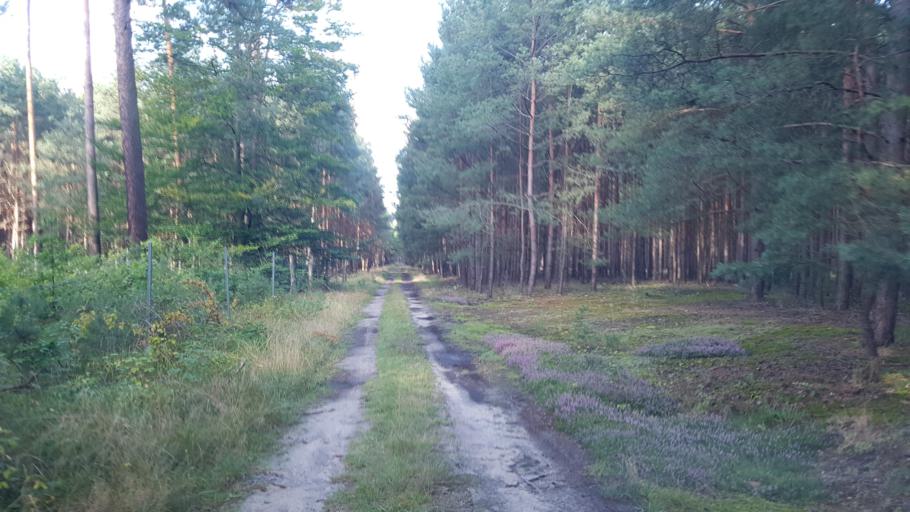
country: DE
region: Brandenburg
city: Schonewalde
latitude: 51.7065
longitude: 13.5870
